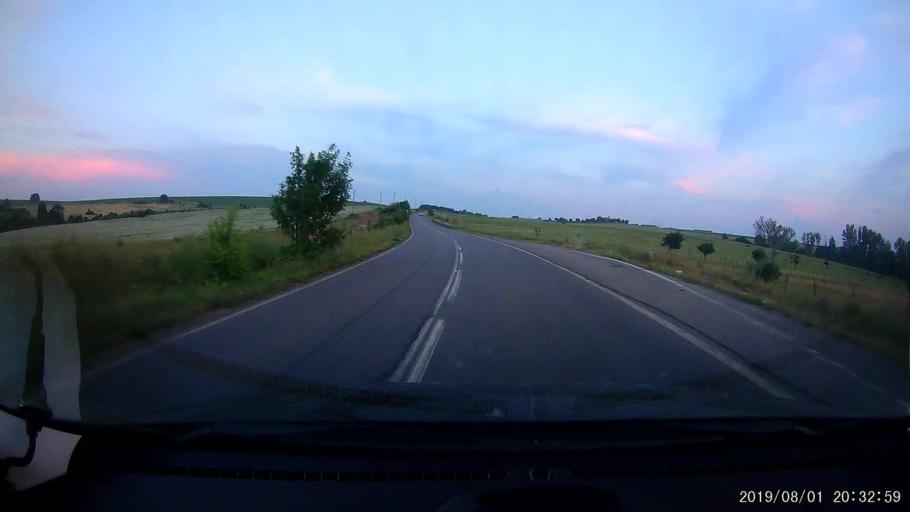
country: BG
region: Yambol
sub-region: Obshtina Elkhovo
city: Elkhovo
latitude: 42.1132
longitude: 26.5310
